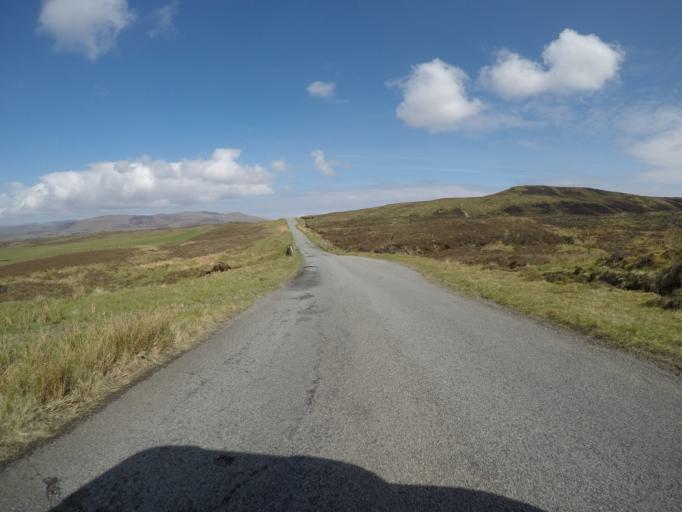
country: GB
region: Scotland
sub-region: Highland
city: Isle of Skye
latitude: 57.4210
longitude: -6.2836
